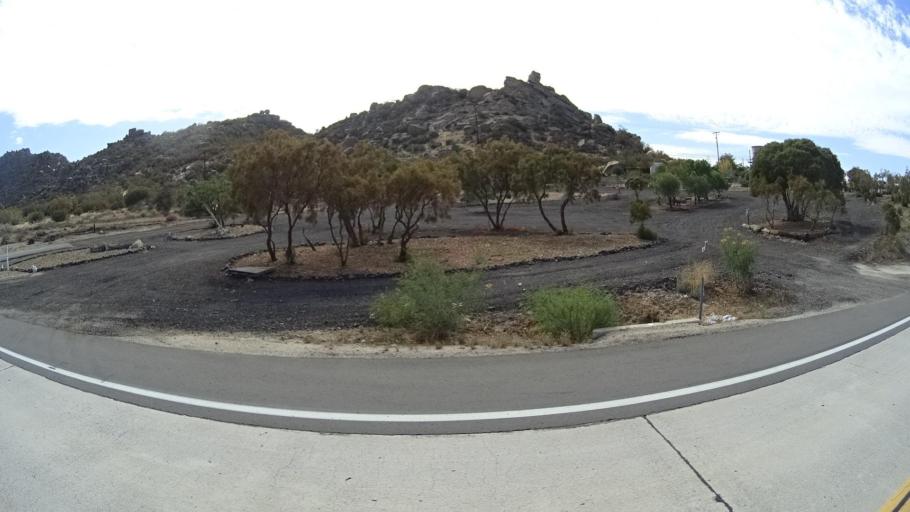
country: MX
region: Baja California
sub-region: Tecate
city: Cereso del Hongo
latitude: 32.6586
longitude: -116.2493
